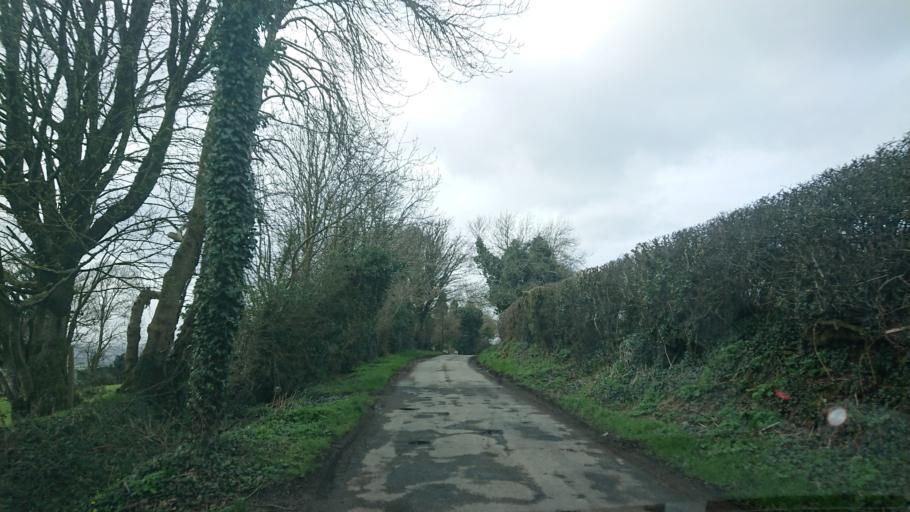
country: IE
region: Leinster
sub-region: Kildare
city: Eadestown
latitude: 53.1590
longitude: -6.5857
